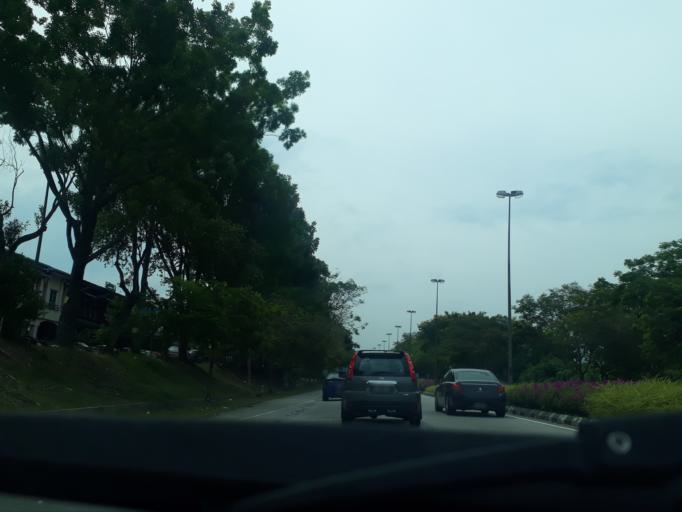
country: MY
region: Perak
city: Ipoh
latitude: 4.6319
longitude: 101.1539
